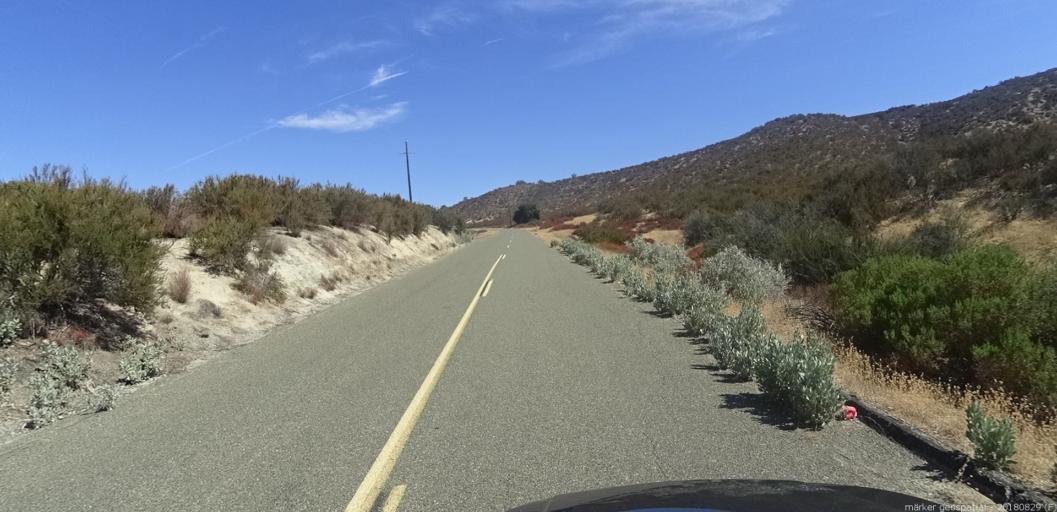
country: US
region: California
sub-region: San Luis Obispo County
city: Lake Nacimiento
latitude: 35.8162
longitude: -120.9803
